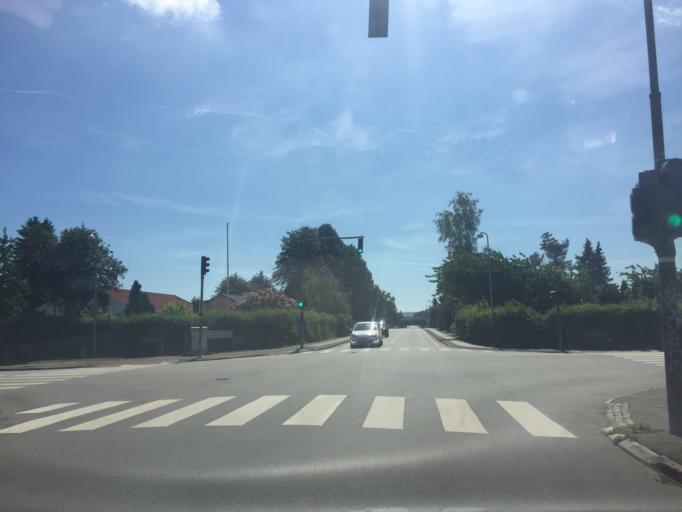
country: DK
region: Capital Region
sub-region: Hoje-Taastrup Kommune
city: Flong
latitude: 55.6589
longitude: 12.1843
